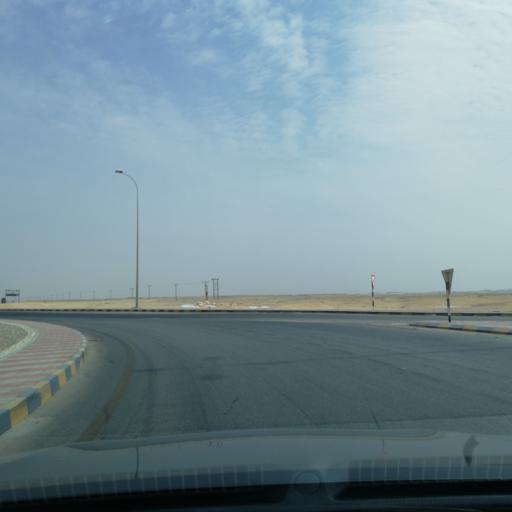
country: OM
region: Zufar
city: Salalah
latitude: 17.6564
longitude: 54.0576
